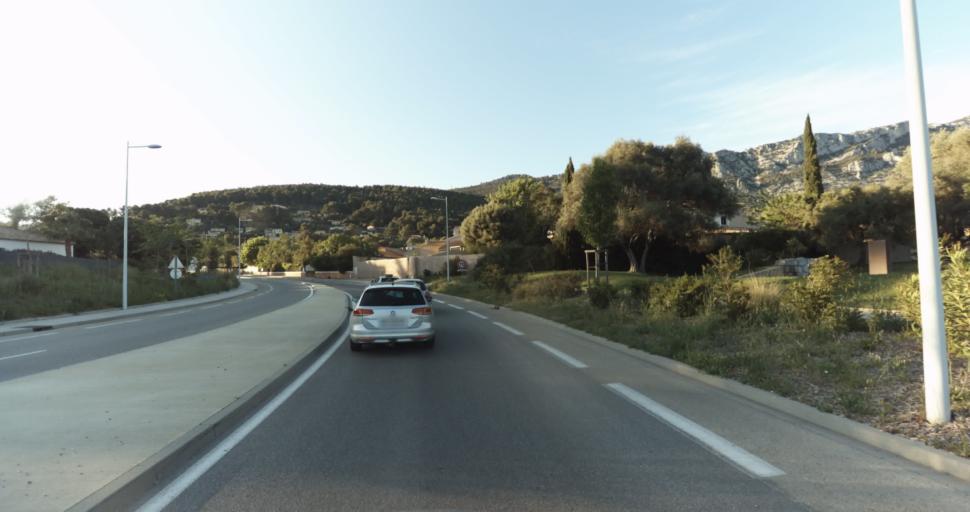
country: FR
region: Provence-Alpes-Cote d'Azur
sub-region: Departement du Var
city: La Valette-du-Var
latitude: 43.1459
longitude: 5.9829
